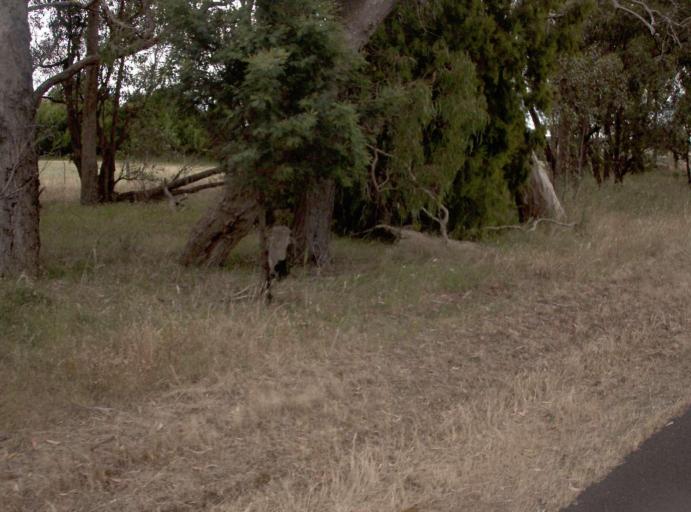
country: AU
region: Victoria
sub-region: Wellington
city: Sale
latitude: -38.3680
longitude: 146.9883
